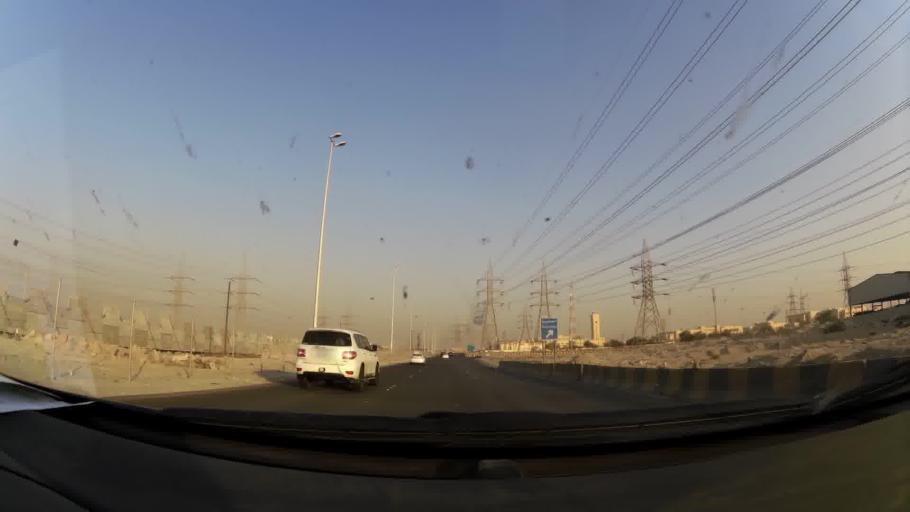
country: KW
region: Al Asimah
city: Ar Rabiyah
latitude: 29.2948
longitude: 47.8493
